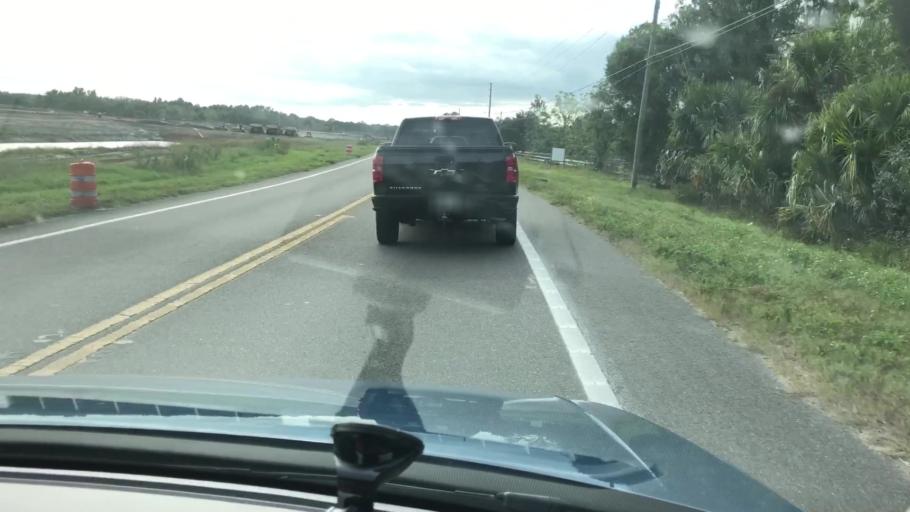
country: US
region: Florida
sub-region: Seminole County
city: Heathrow
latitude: 28.8153
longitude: -81.4341
